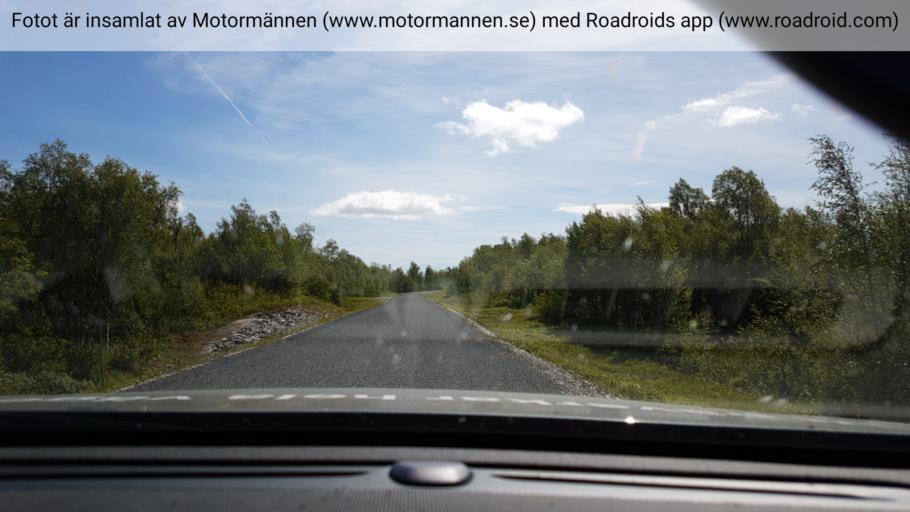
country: NO
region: Nordland
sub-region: Hattfjelldal
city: Hattfjelldal
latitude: 65.4091
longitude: 14.9407
